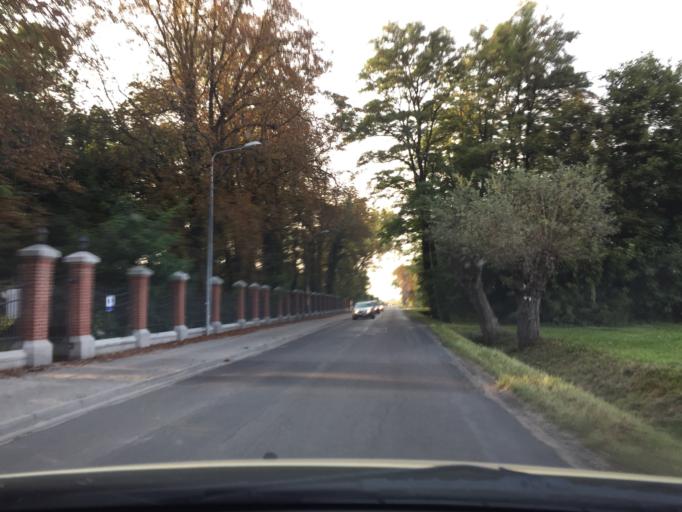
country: PL
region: Greater Poland Voivodeship
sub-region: Powiat poznanski
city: Plewiska
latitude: 52.3688
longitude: 16.8066
